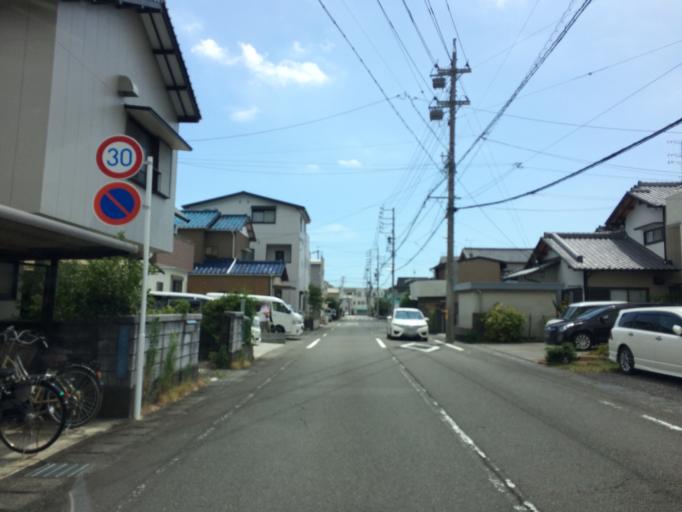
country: JP
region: Shizuoka
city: Yaizu
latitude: 34.8756
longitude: 138.3154
